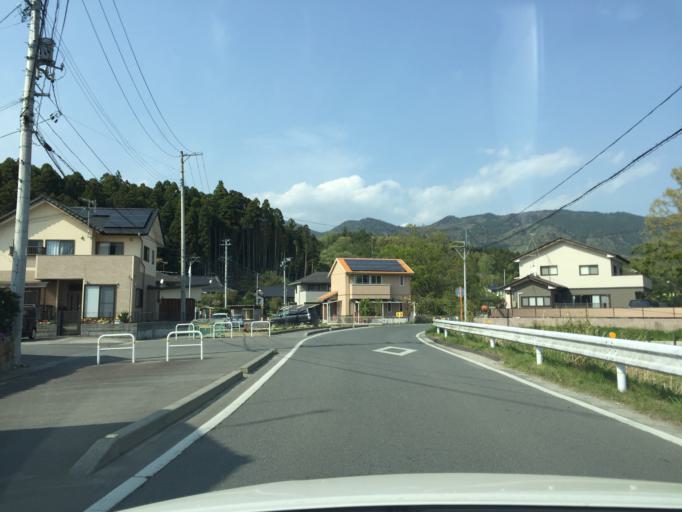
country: JP
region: Fukushima
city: Iwaki
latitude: 37.1350
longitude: 140.8635
